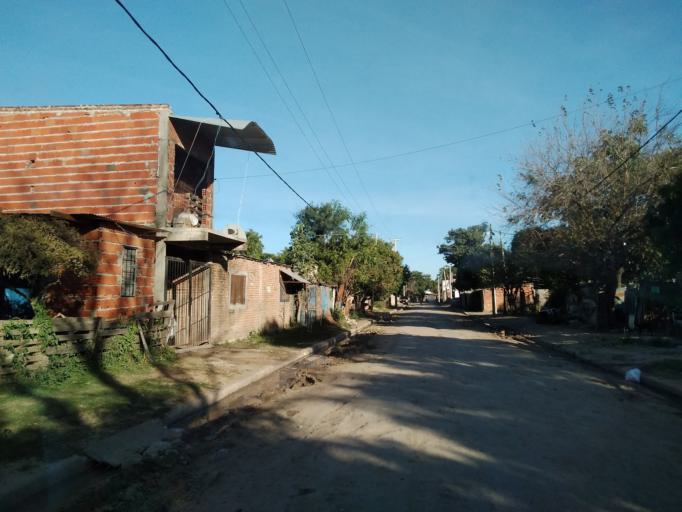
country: AR
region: Corrientes
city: Corrientes
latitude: -27.5012
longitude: -58.8364
